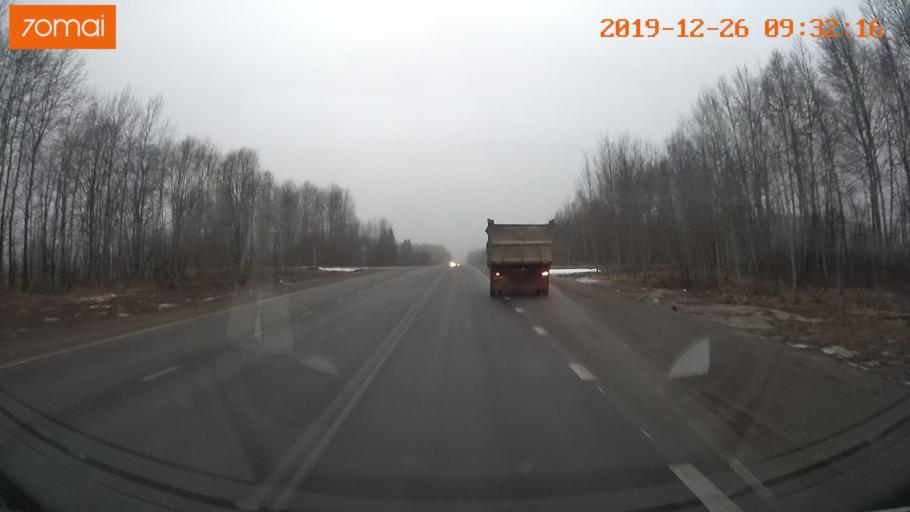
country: RU
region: Vologda
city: Gryazovets
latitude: 59.0761
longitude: 40.1188
